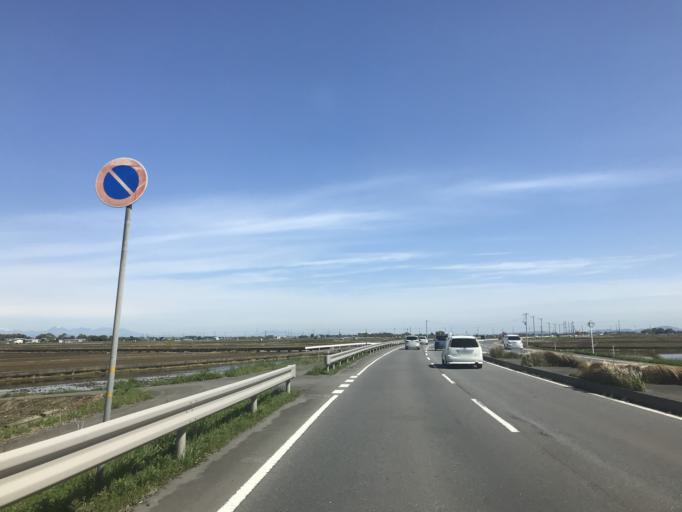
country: JP
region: Ibaraki
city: Ishige
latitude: 36.1269
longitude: 139.9820
